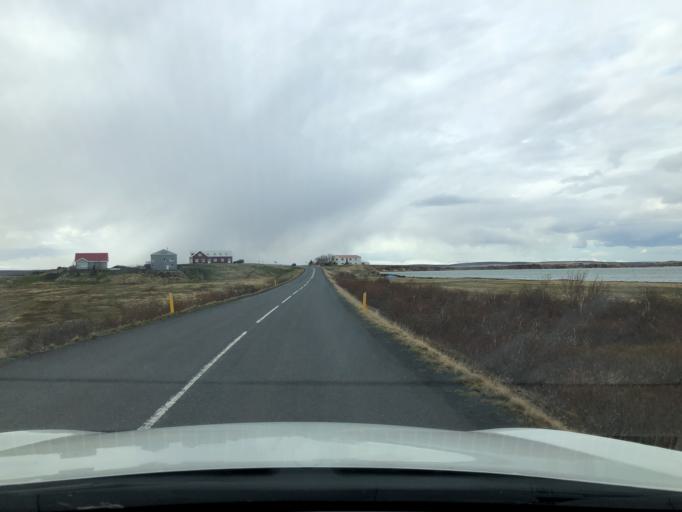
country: IS
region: Northeast
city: Laugar
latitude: 65.5682
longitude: -17.0410
